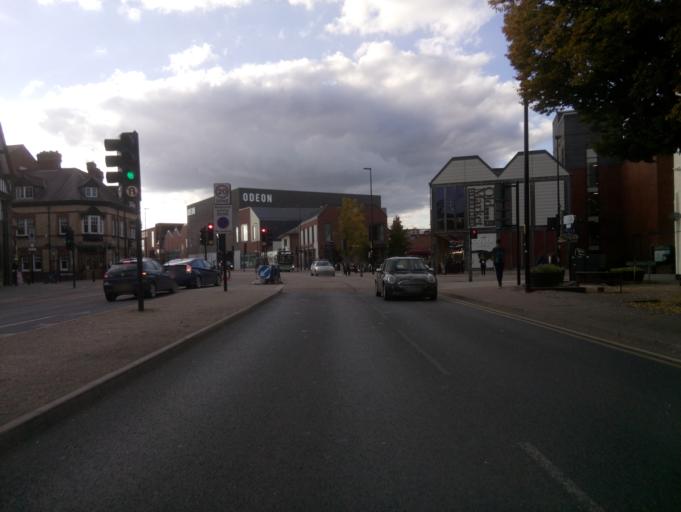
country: GB
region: England
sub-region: Herefordshire
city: Hereford
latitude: 52.0584
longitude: -2.7154
